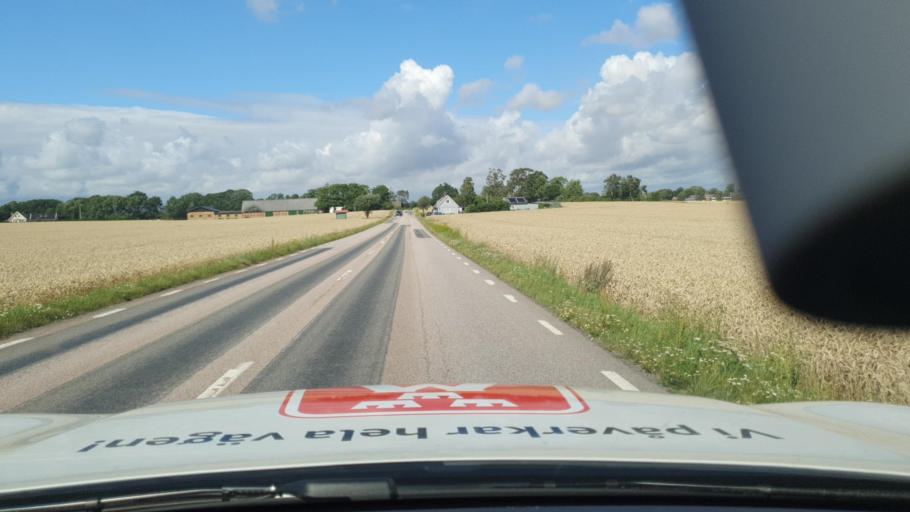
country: SE
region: Skane
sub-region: Angelholms Kommun
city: Strovelstorp
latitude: 56.1550
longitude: 12.8259
